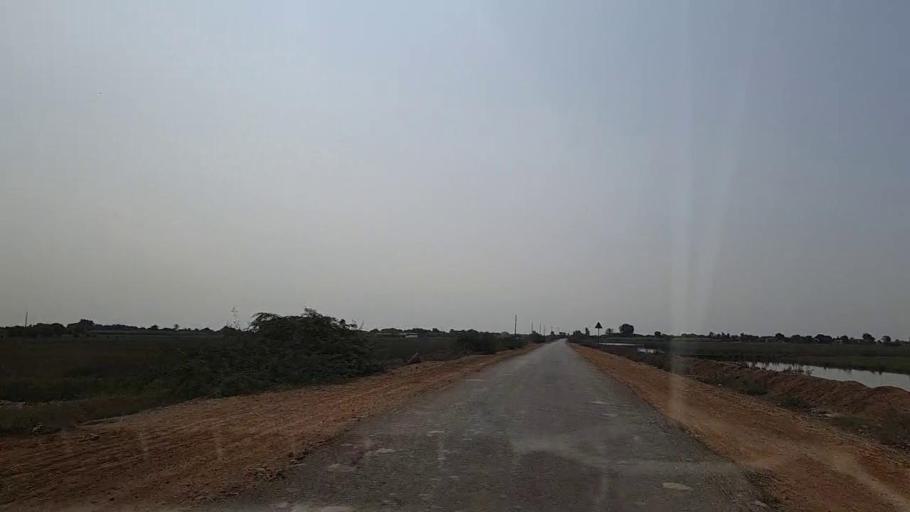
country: PK
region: Sindh
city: Chuhar Jamali
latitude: 24.3099
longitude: 67.9387
